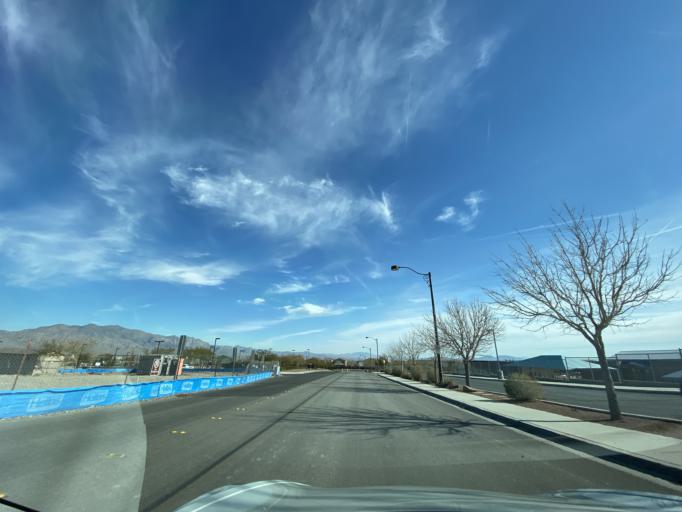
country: US
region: Nevada
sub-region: Clark County
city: Summerlin South
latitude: 36.2975
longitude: -115.3218
